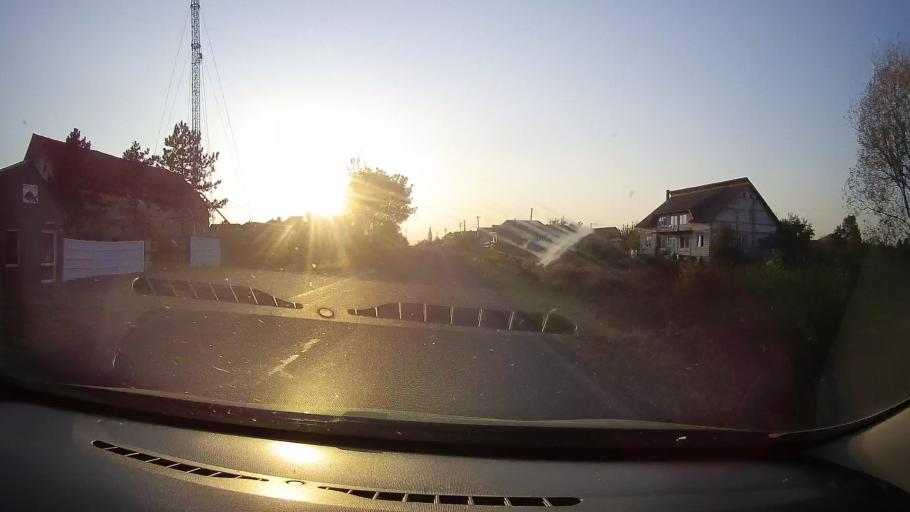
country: RO
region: Arad
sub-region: Comuna Bocsig
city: Bocsig
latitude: 46.4227
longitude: 21.9496
